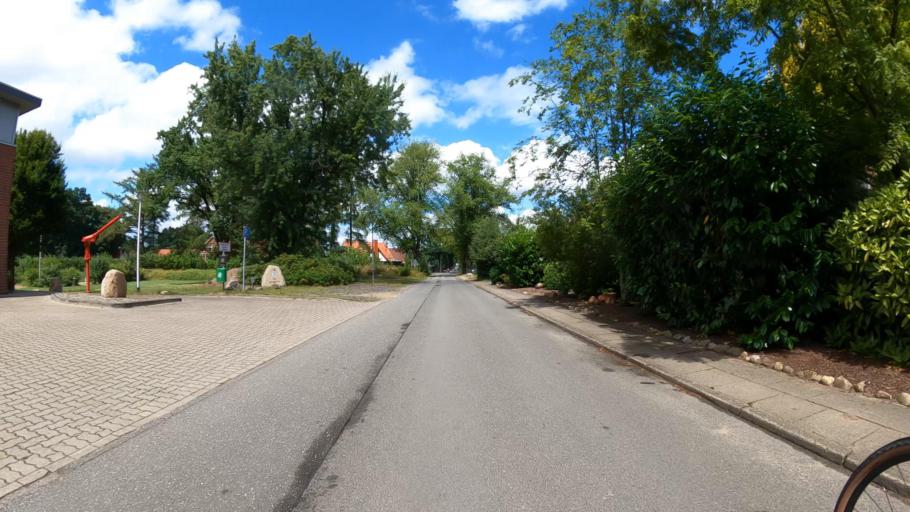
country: DE
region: Lower Saxony
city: Neu Wulmstorf
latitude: 53.4501
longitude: 9.7561
